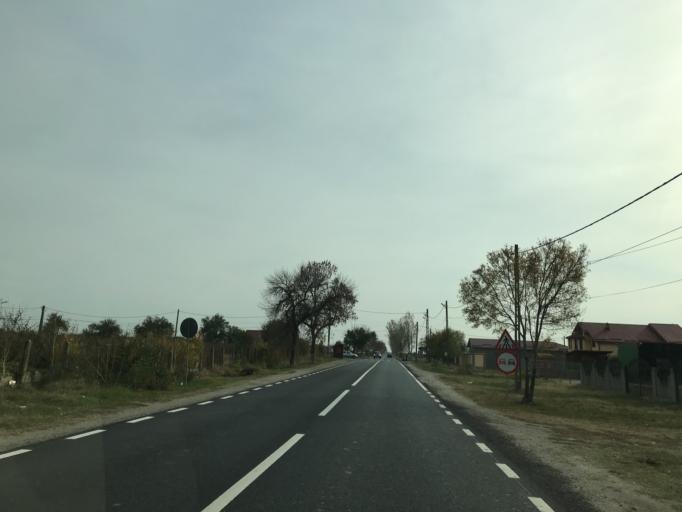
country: RO
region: Olt
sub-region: Comuna Brancoveni
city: Brancoveni
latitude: 44.3151
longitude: 24.2985
